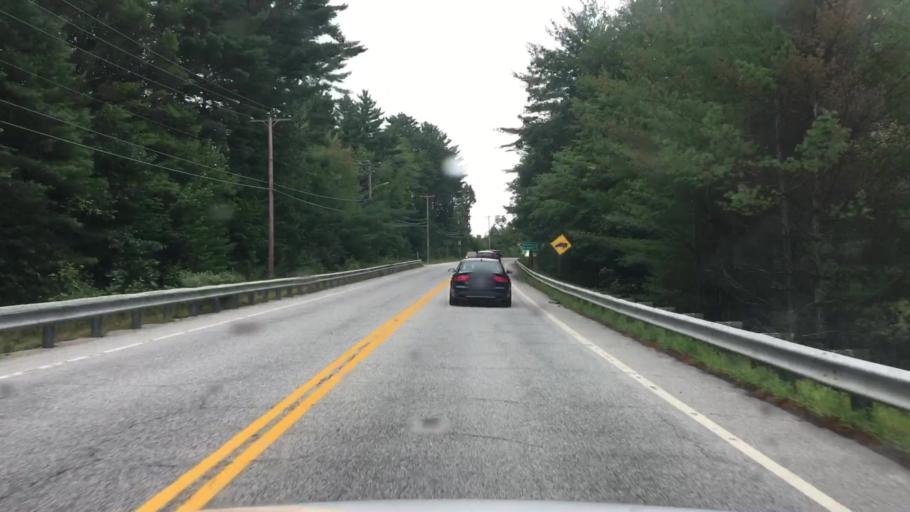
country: US
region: Maine
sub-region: York County
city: Cornish
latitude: 43.8410
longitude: -70.7815
